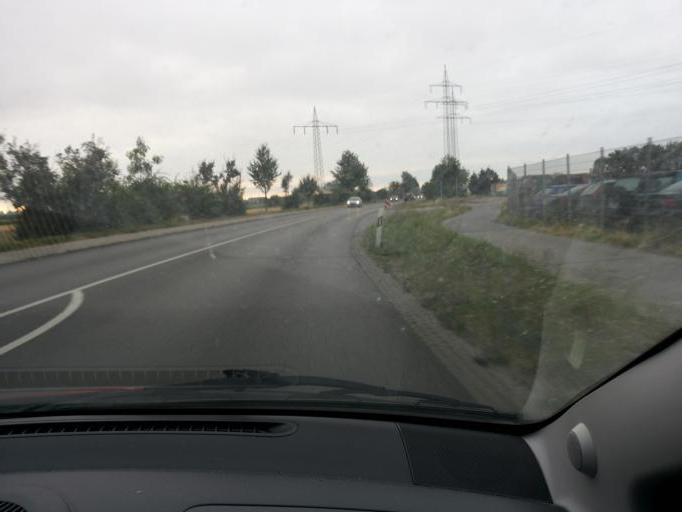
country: DE
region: Bavaria
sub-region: Upper Bavaria
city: Gaimersheim
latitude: 48.7901
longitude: 11.3827
